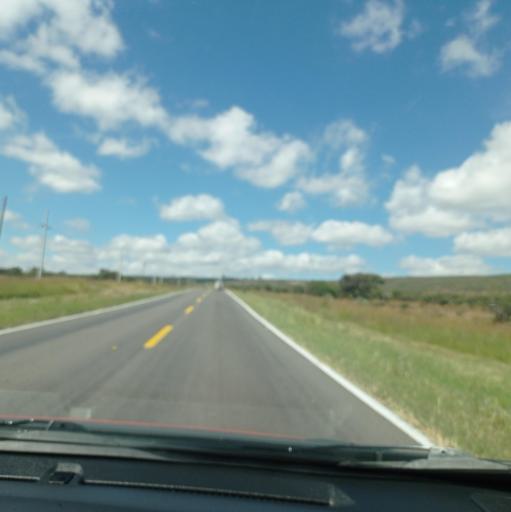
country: MX
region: Jalisco
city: San Miguel el Alto
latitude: 21.0175
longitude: -102.5005
